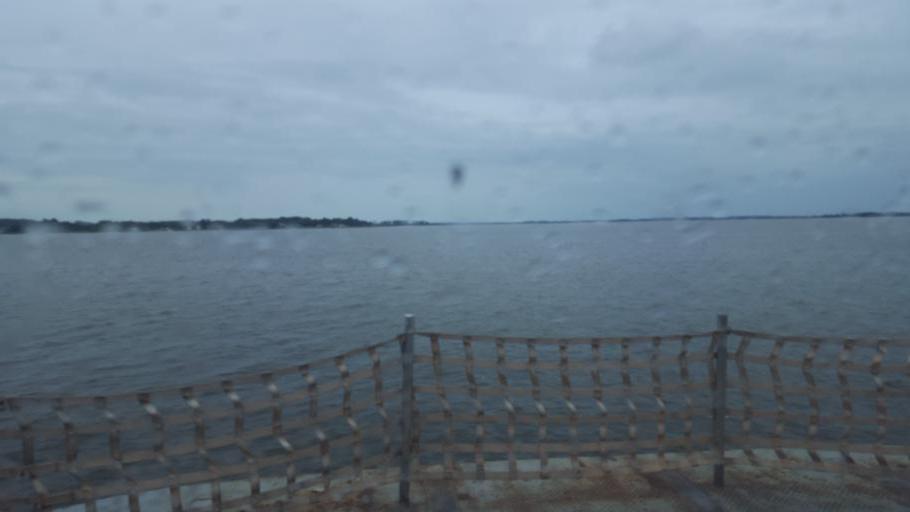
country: US
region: North Carolina
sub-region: Currituck County
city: Currituck
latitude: 36.4780
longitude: -75.9372
